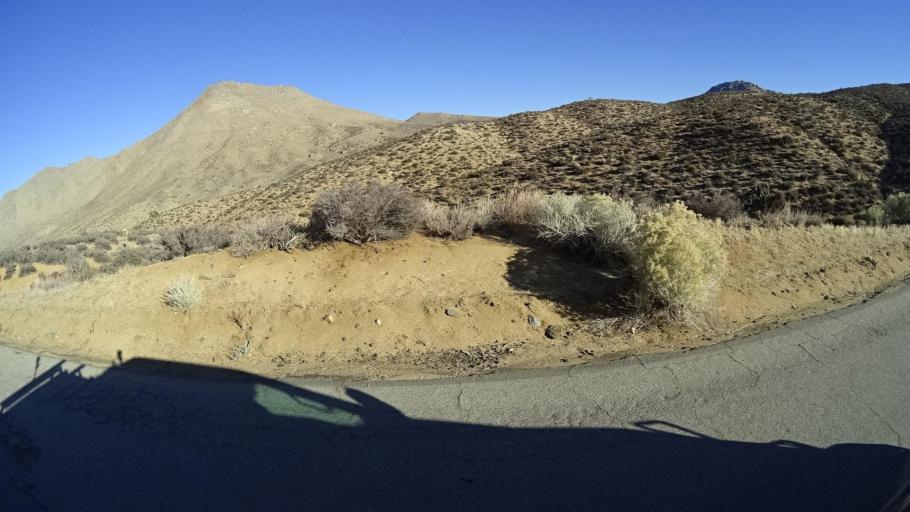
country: US
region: California
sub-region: Kern County
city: Weldon
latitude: 35.4568
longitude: -118.2161
